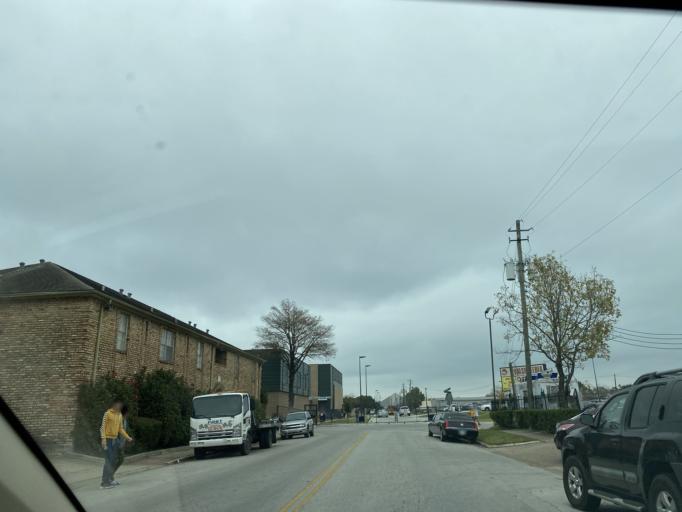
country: US
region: Texas
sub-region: Harris County
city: Piney Point Village
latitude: 29.7277
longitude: -95.4979
